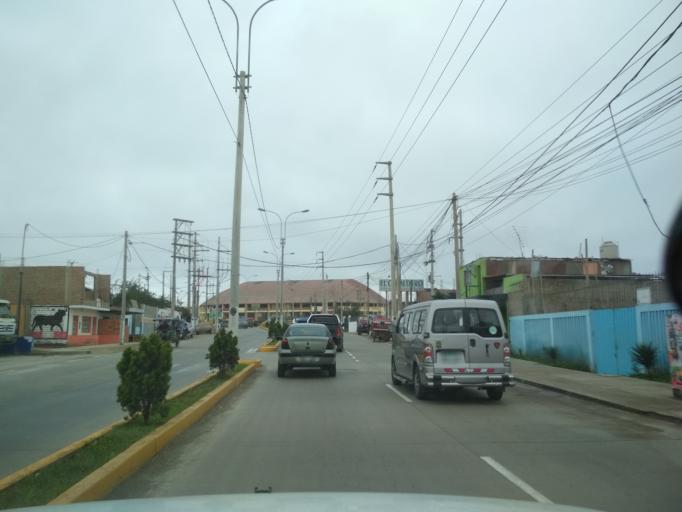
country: PE
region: Lima
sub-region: Provincia de Canete
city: San Vicente de Canete
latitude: -13.0742
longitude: -76.3709
